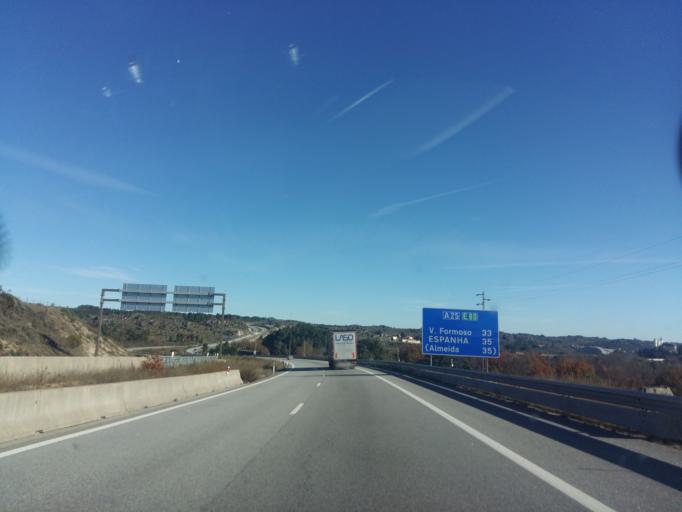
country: PT
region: Guarda
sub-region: Guarda
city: Sequeira
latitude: 40.5738
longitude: -7.1969
